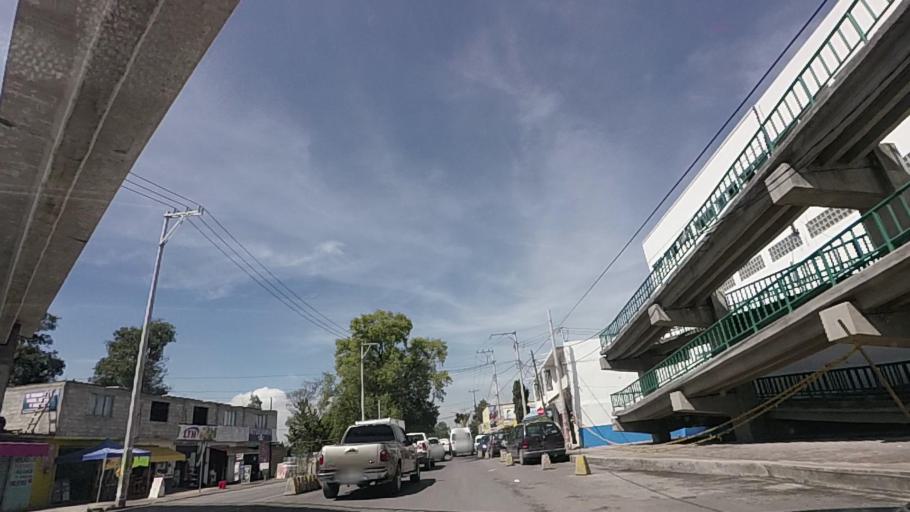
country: MX
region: Mexico
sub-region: Cuautitlan
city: Barrio Tlatenco
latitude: 19.7338
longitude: -99.1846
